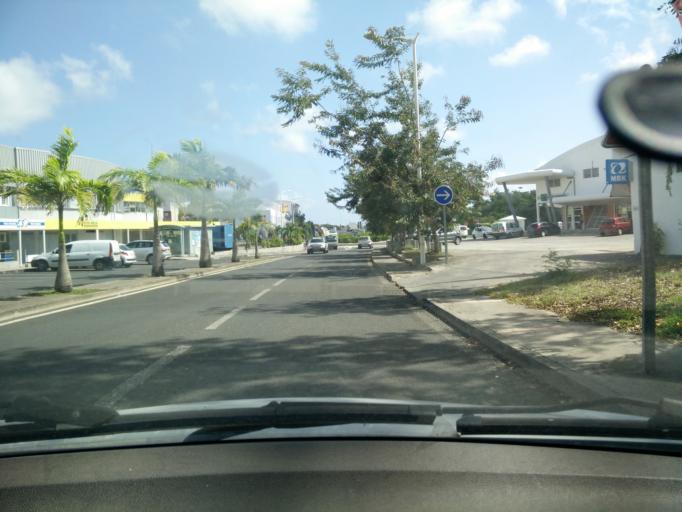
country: GP
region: Guadeloupe
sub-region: Guadeloupe
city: Le Moule
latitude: 16.3300
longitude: -61.3556
